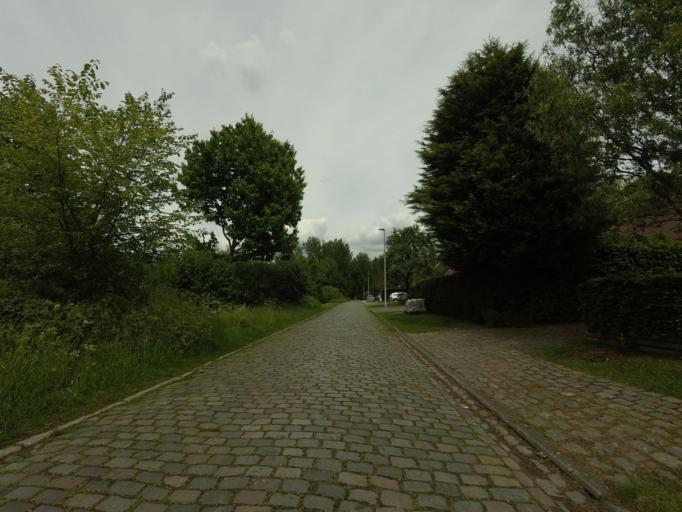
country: BE
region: Flanders
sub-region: Provincie Antwerpen
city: Bornem
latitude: 51.1073
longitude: 4.2602
